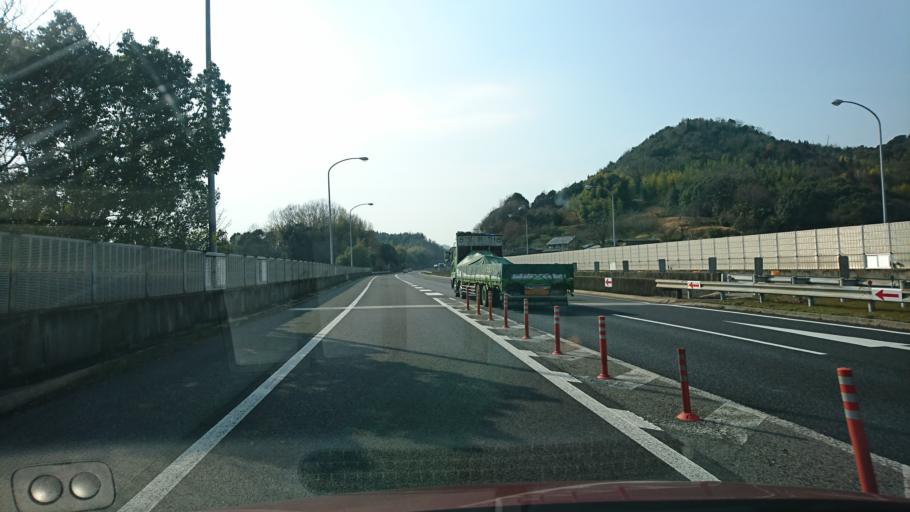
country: JP
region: Hiroshima
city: Fukuyama
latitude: 34.4883
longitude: 133.3142
